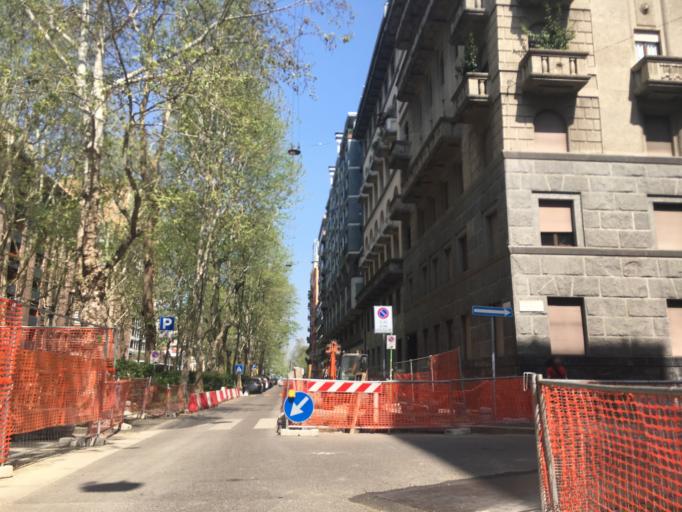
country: IT
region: Lombardy
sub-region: Citta metropolitana di Milano
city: Milano
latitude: 45.4726
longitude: 9.1486
